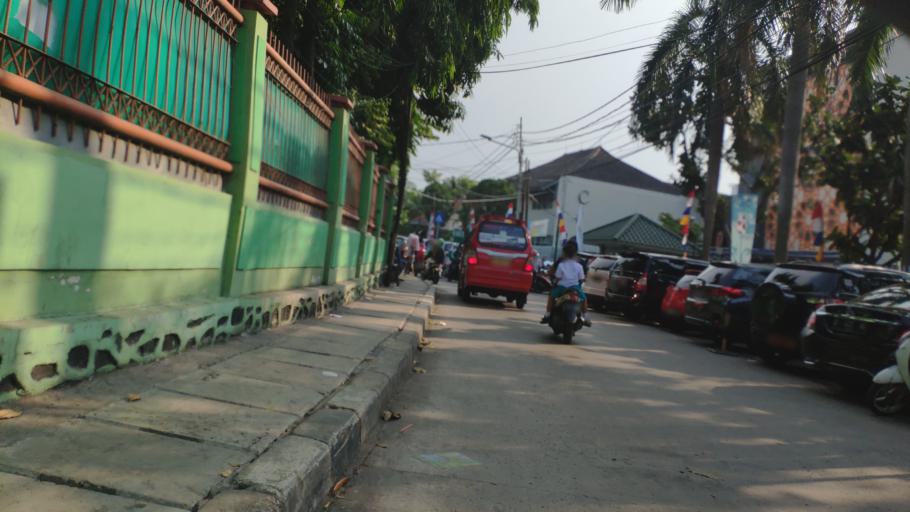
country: ID
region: Jakarta Raya
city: Jakarta
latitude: -6.2784
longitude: 106.7996
